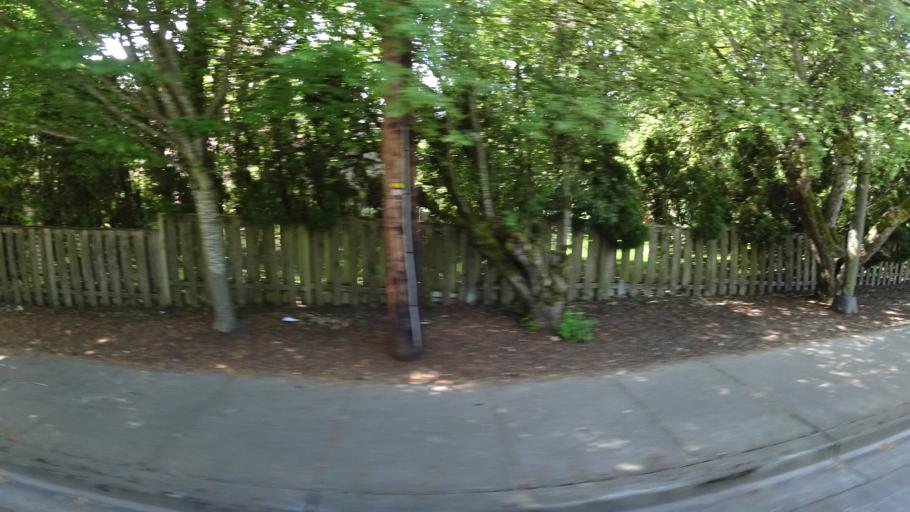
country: US
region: Oregon
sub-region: Washington County
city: Beaverton
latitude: 45.4751
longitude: -122.8367
